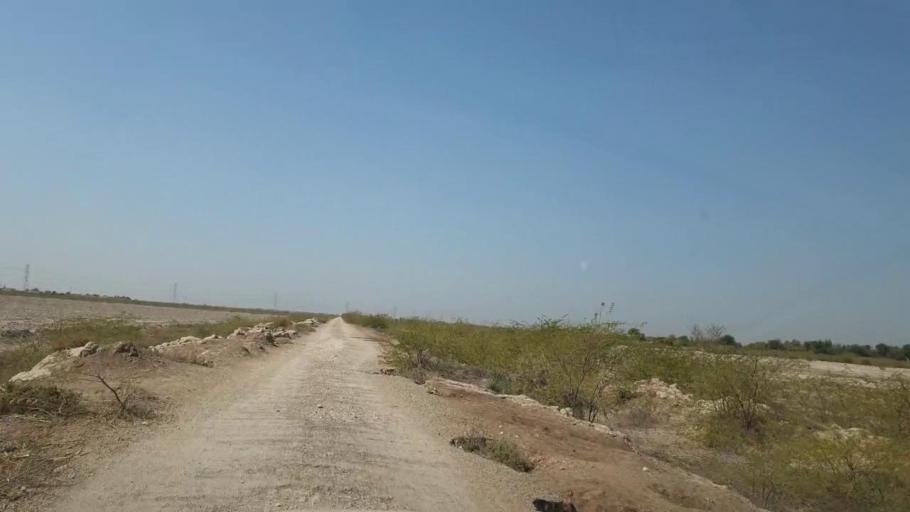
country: PK
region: Sindh
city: Kunri
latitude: 25.0964
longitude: 69.5028
